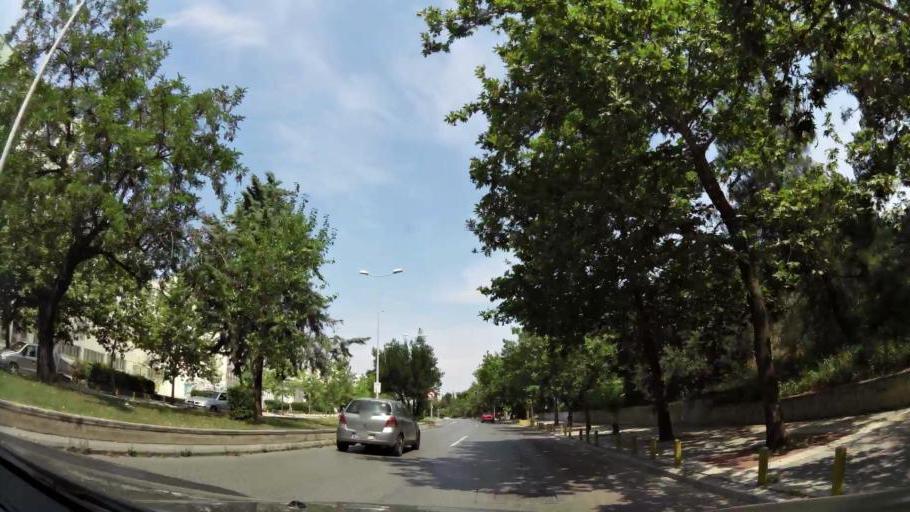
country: GR
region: Central Macedonia
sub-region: Nomos Thessalonikis
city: Agios Pavlos
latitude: 40.6316
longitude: 22.9608
